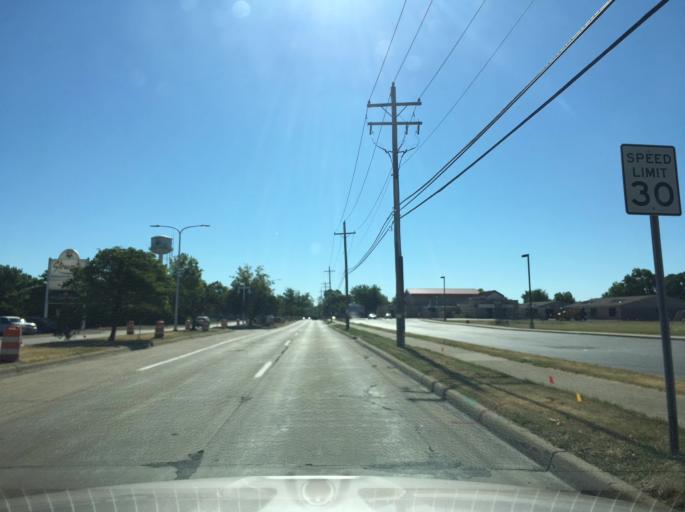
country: US
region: Michigan
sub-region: Macomb County
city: Saint Clair Shores
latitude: 42.5320
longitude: -82.8958
